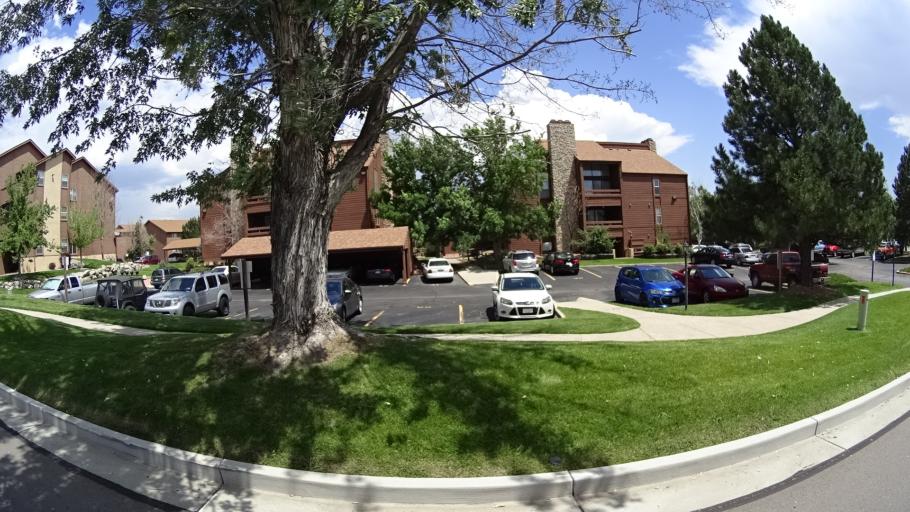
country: US
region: Colorado
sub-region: El Paso County
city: Air Force Academy
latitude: 38.9292
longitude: -104.8310
